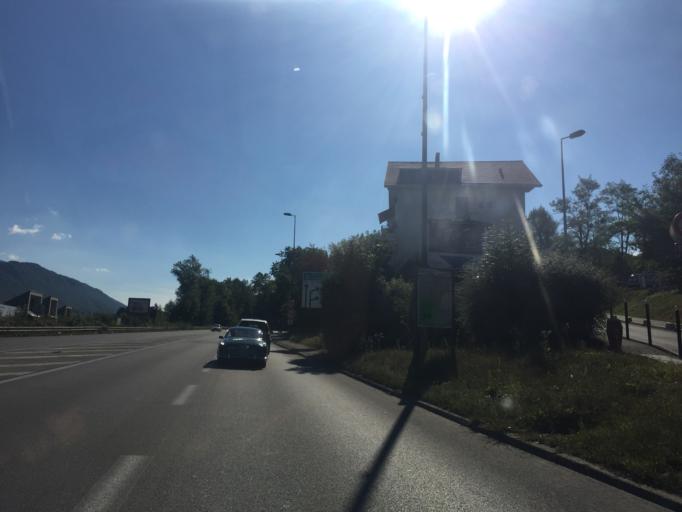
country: FR
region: Rhone-Alpes
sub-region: Departement de la Haute-Savoie
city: Annecy
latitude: 45.8917
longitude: 6.1101
